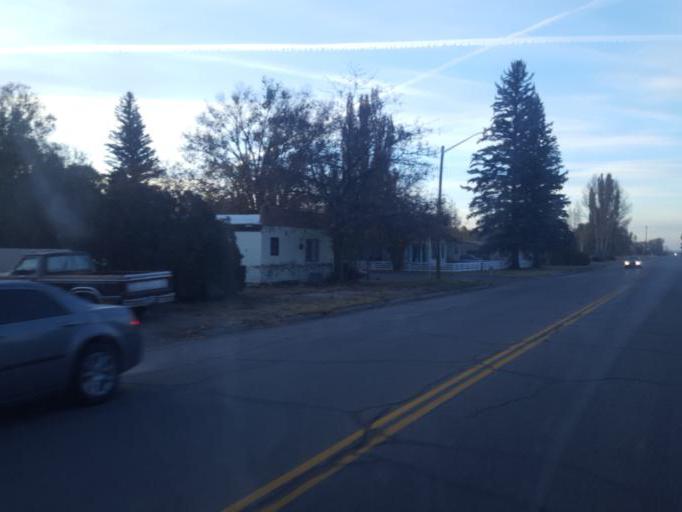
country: US
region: Colorado
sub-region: Rio Grande County
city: Monte Vista
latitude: 37.5773
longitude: -106.1495
